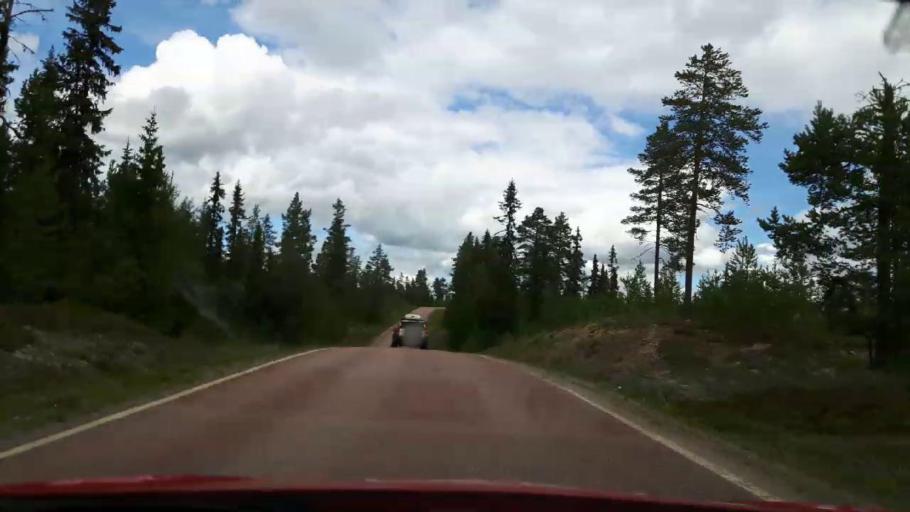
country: NO
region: Hedmark
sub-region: Trysil
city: Innbygda
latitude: 61.8705
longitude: 12.9601
